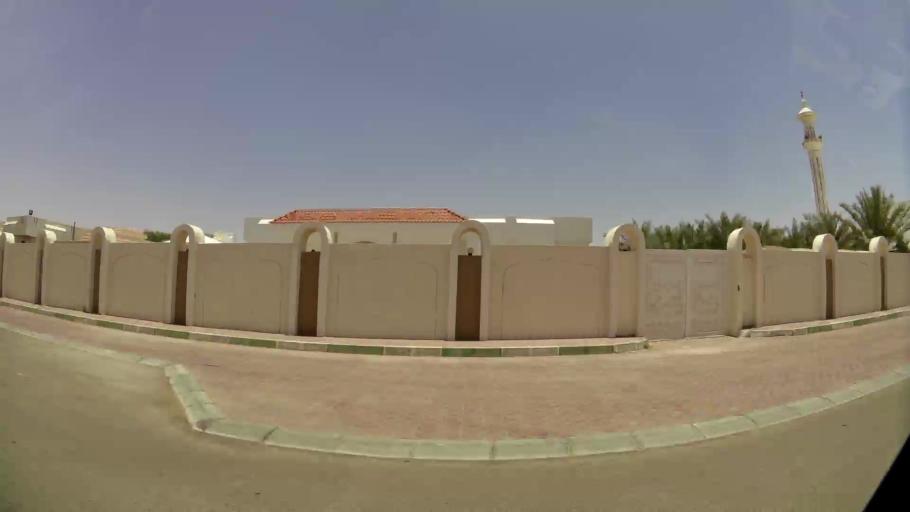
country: OM
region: Al Buraimi
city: Al Buraymi
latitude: 24.2661
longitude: 55.7243
